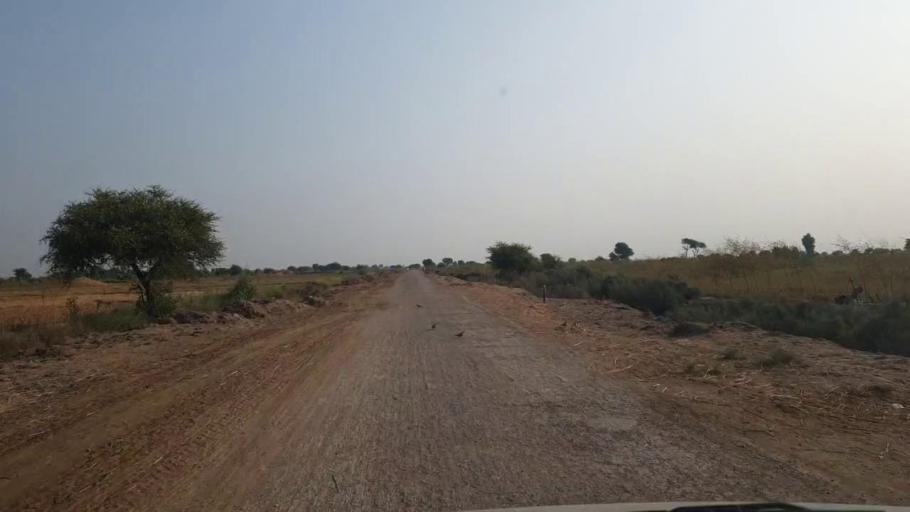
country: PK
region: Sindh
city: Matli
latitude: 25.0587
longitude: 68.7620
